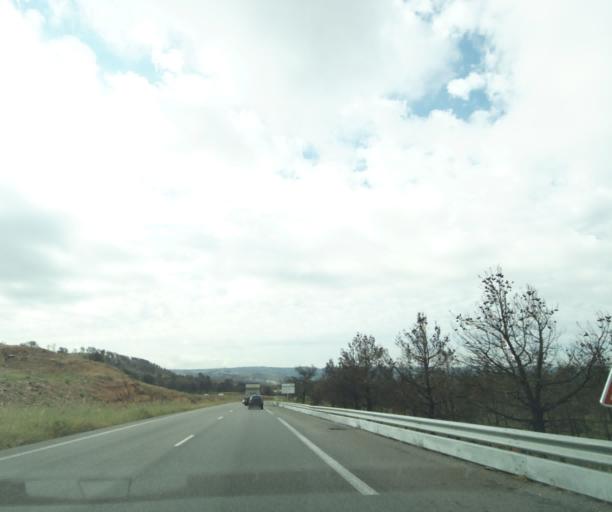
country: FR
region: Provence-Alpes-Cote d'Azur
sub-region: Departement des Bouches-du-Rhone
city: Les Pennes-Mirabeau
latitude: 43.4479
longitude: 5.2977
